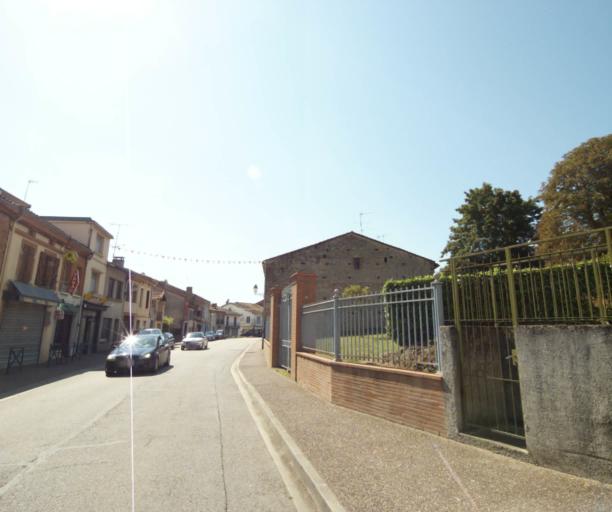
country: FR
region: Midi-Pyrenees
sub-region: Departement de l'Ariege
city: Lezat-sur-Leze
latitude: 43.2769
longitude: 1.3474
